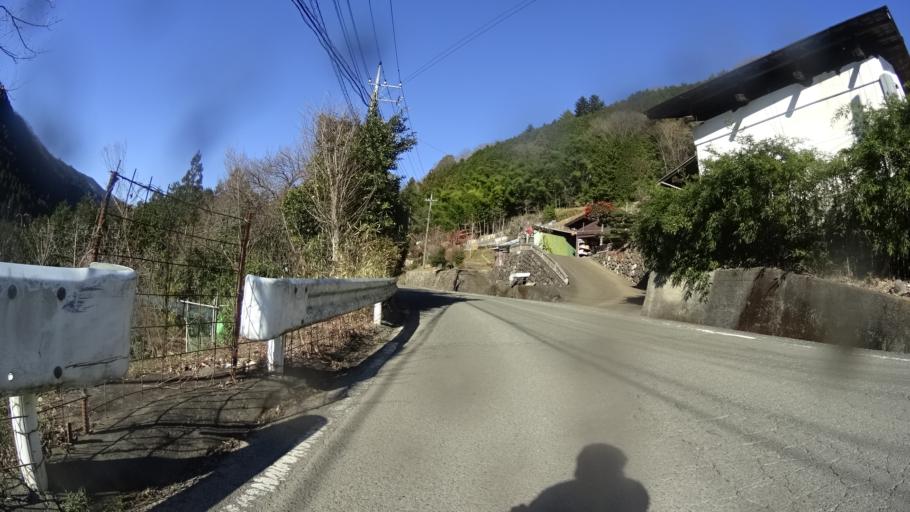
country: JP
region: Yamanashi
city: Uenohara
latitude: 35.6787
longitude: 139.0749
